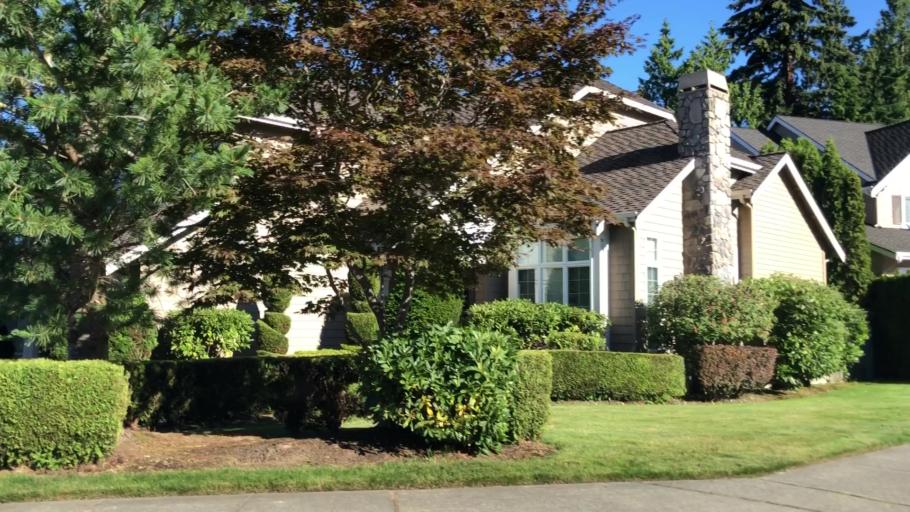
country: US
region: Washington
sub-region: Snohomish County
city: North Creek
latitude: 47.8155
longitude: -122.1978
